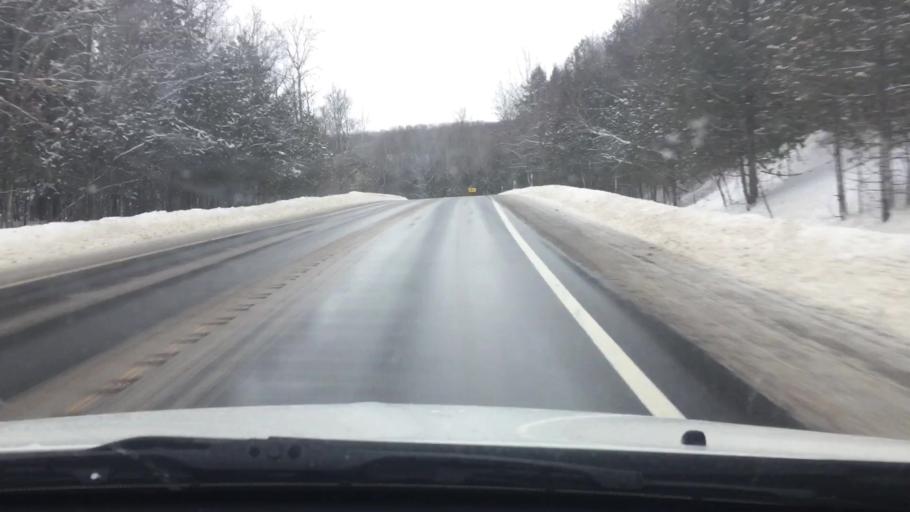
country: US
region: Michigan
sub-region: Charlevoix County
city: East Jordan
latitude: 45.1306
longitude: -85.0810
